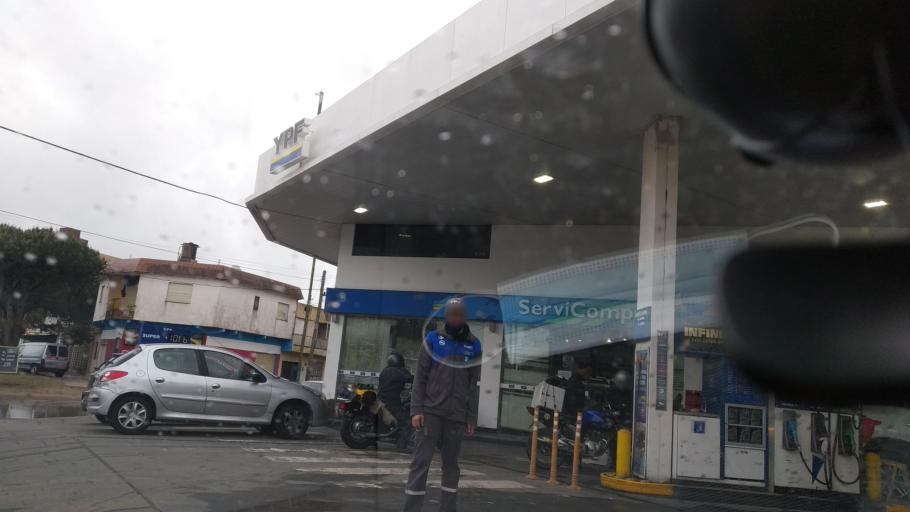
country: AR
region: Buenos Aires
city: San Clemente del Tuyu
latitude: -36.3732
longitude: -56.7178
